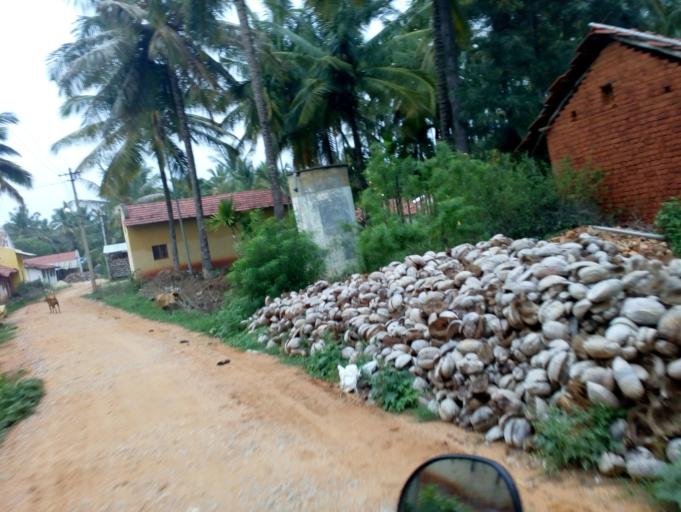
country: IN
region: Karnataka
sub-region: Tumkur
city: Turuvekere
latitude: 13.1937
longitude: 76.7243
